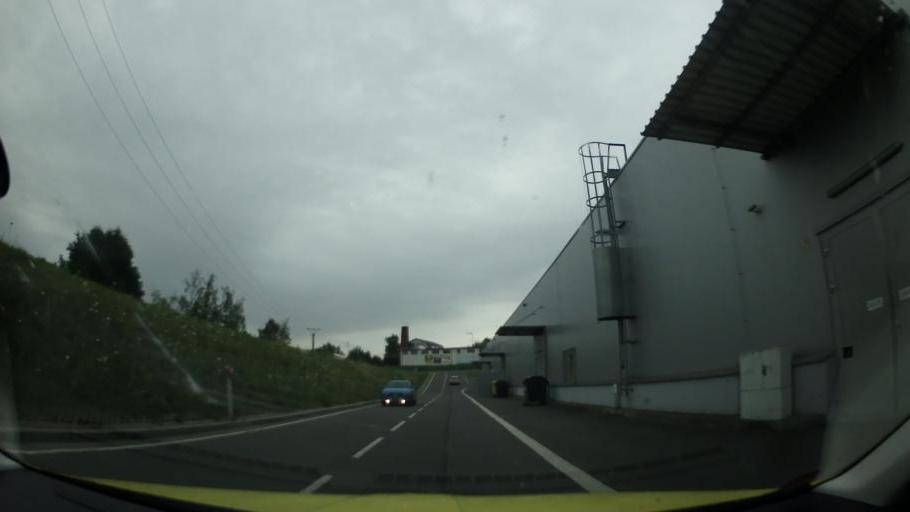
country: CZ
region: Olomoucky
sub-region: Okres Prerov
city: Hranice
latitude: 49.5585
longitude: 17.7427
